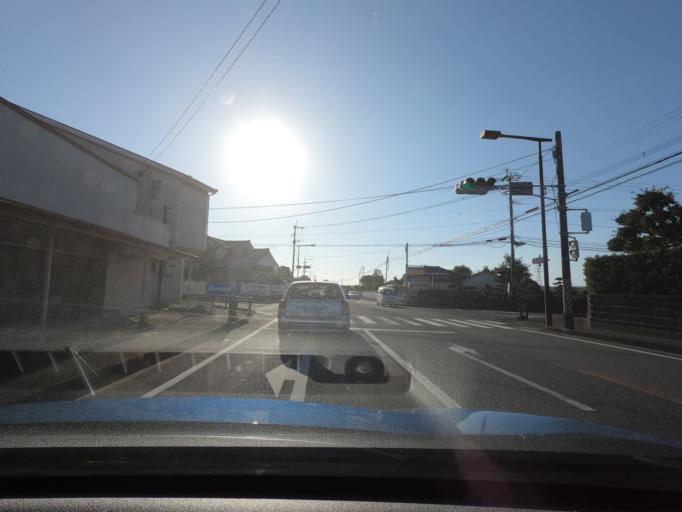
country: JP
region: Kagoshima
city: Izumi
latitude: 32.0938
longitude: 130.2957
